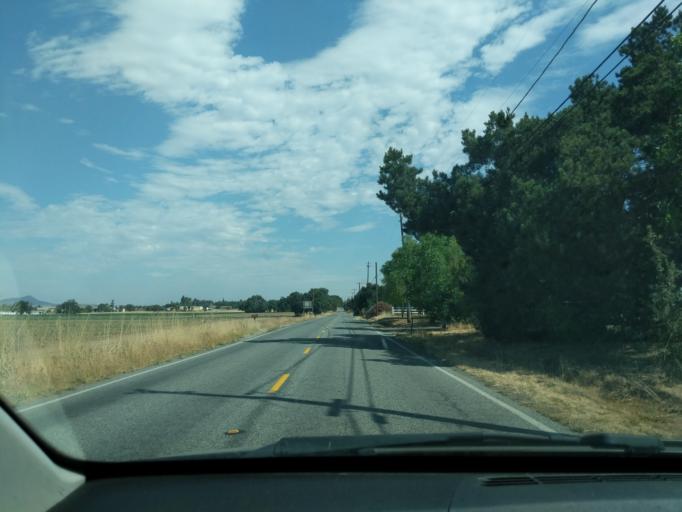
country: US
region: California
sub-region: Santa Clara County
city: Gilroy
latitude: 37.0426
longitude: -121.5424
